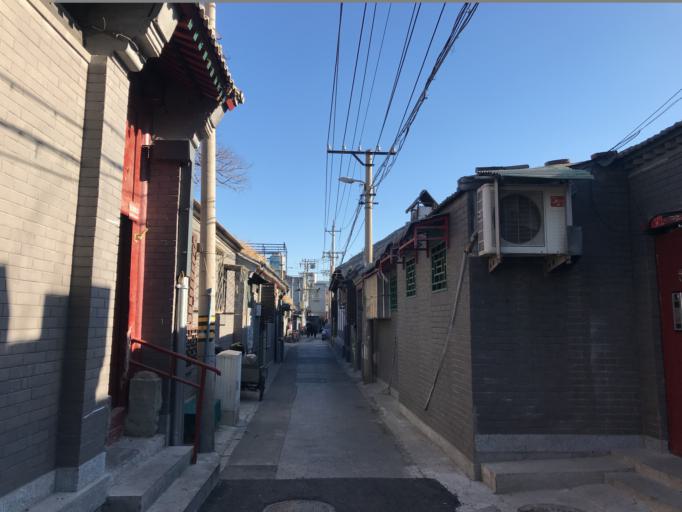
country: CN
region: Beijing
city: Beijing
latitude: 39.8921
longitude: 116.3899
